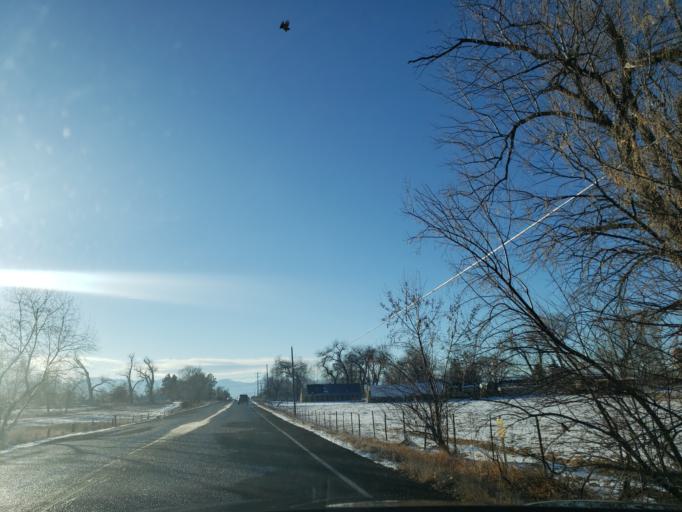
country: US
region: Colorado
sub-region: Larimer County
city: Fort Collins
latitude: 40.6395
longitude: -105.0671
